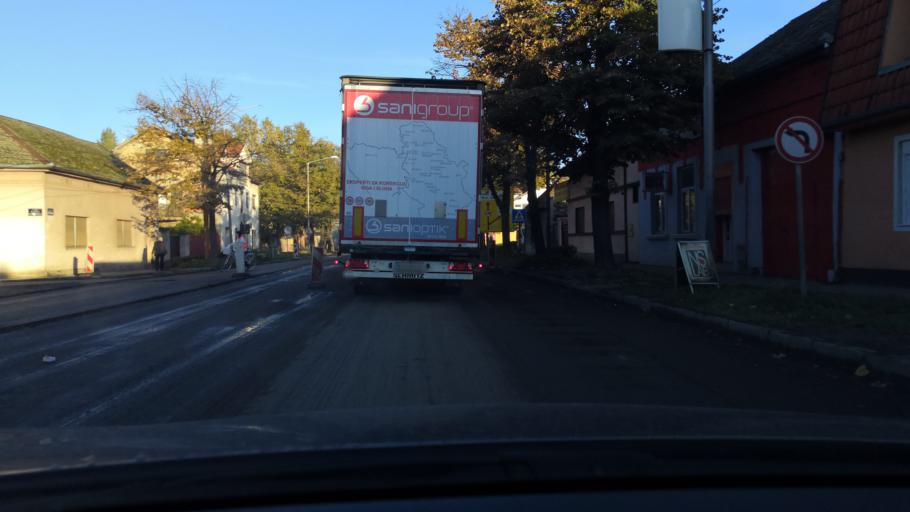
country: RS
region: Autonomna Pokrajina Vojvodina
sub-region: Juznobacki Okrug
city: Petrovaradin
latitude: 45.2472
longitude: 19.8787
